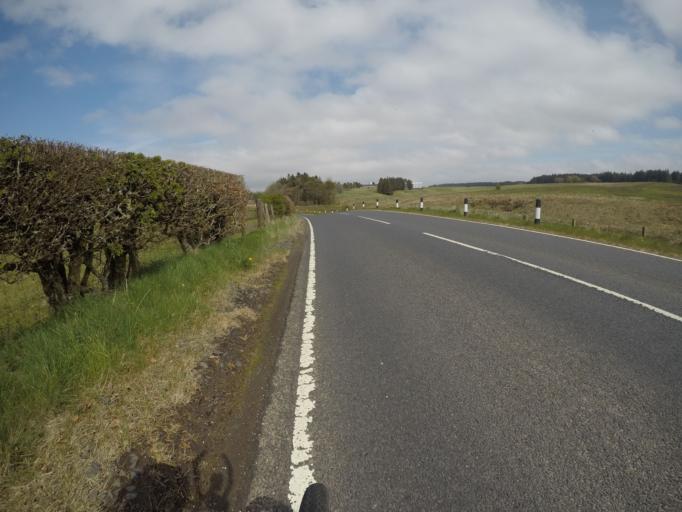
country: GB
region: Scotland
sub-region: East Renfrewshire
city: Neilston
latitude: 55.7175
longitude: -4.4362
